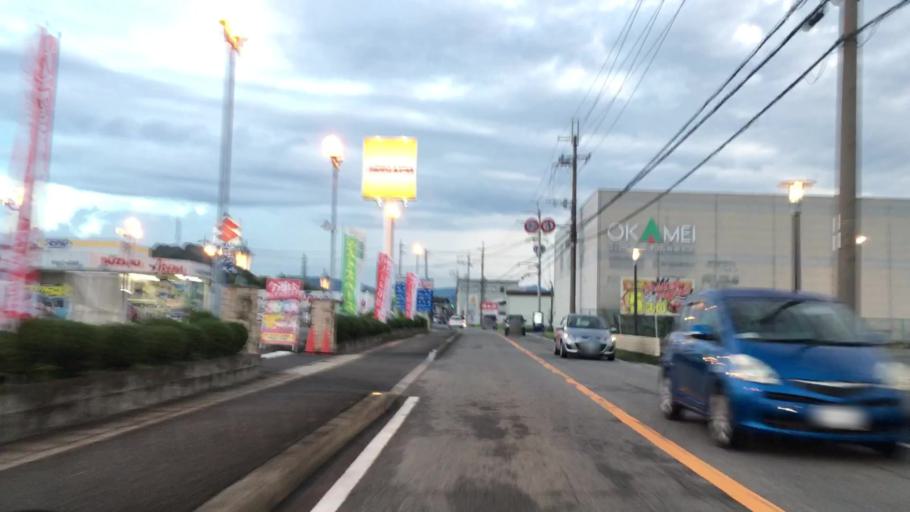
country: JP
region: Hyogo
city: Himeji
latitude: 34.9219
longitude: 134.7433
